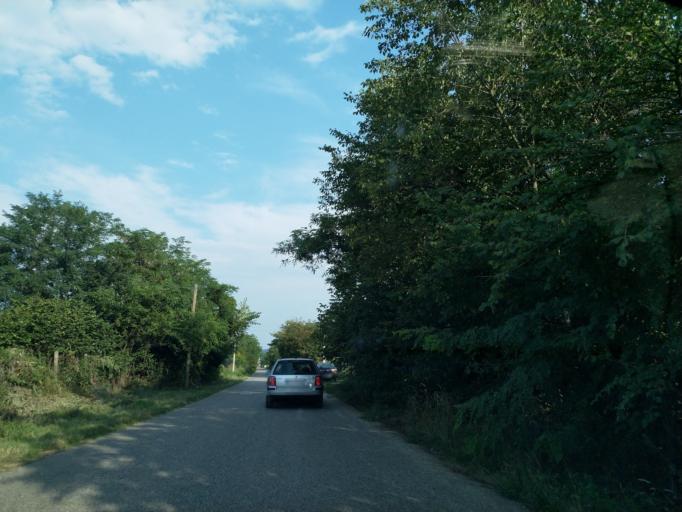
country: RS
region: Central Serbia
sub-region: Pomoravski Okrug
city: Jagodina
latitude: 43.9817
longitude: 21.2247
